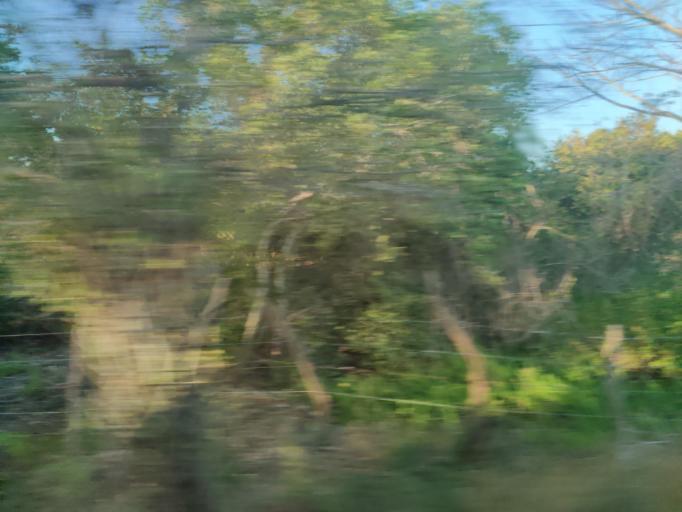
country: CO
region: Atlantico
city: Piojo
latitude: 10.7491
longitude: -75.2497
